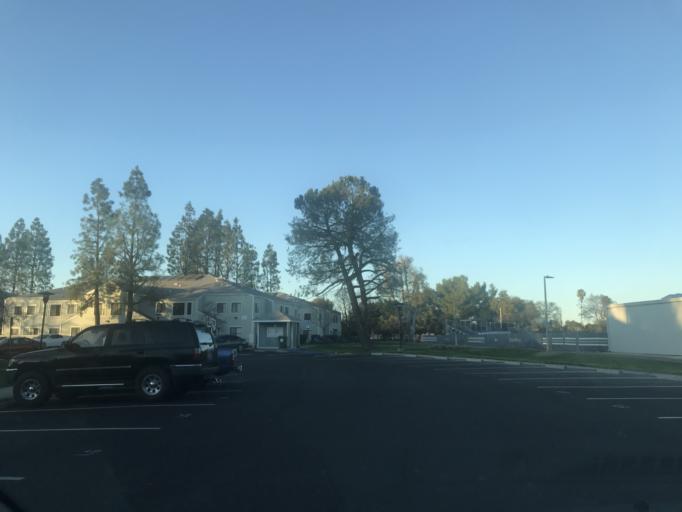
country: US
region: California
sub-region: Yolo County
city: Davis
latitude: 38.5448
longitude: -121.7606
